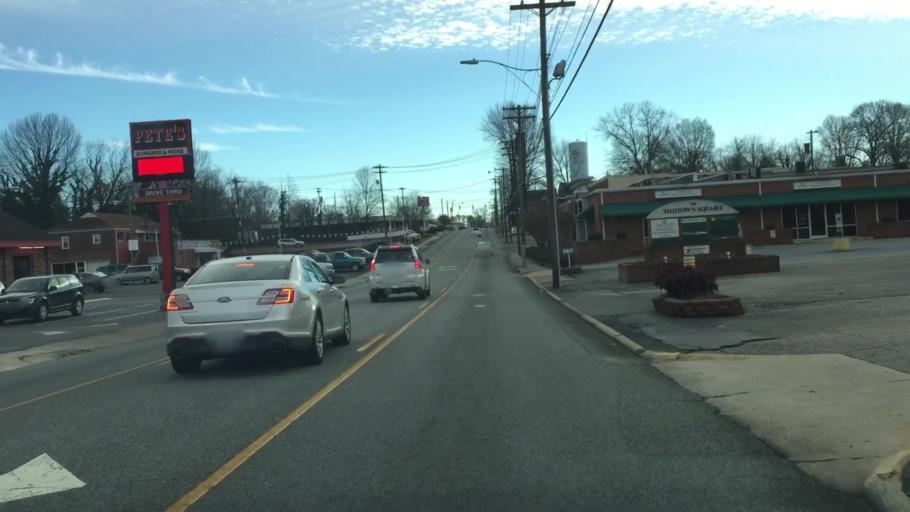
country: US
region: North Carolina
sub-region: Rockingham County
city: Reidsville
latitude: 36.3509
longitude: -79.6649
